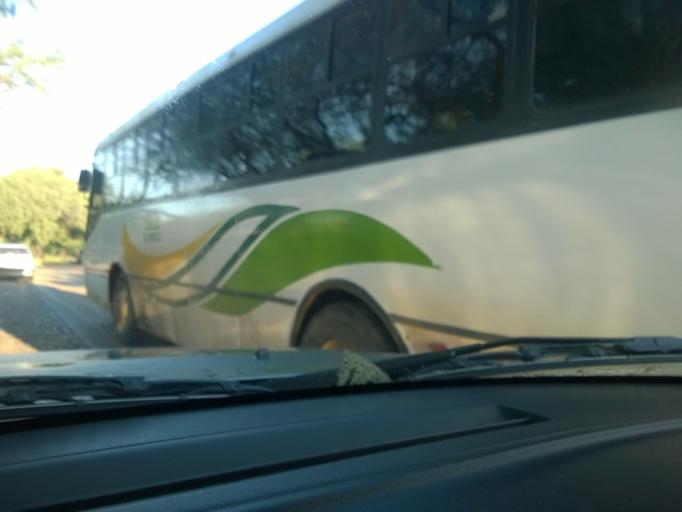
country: MX
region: Guanajuato
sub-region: Leon
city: Medina
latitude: 21.1129
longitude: -101.6205
